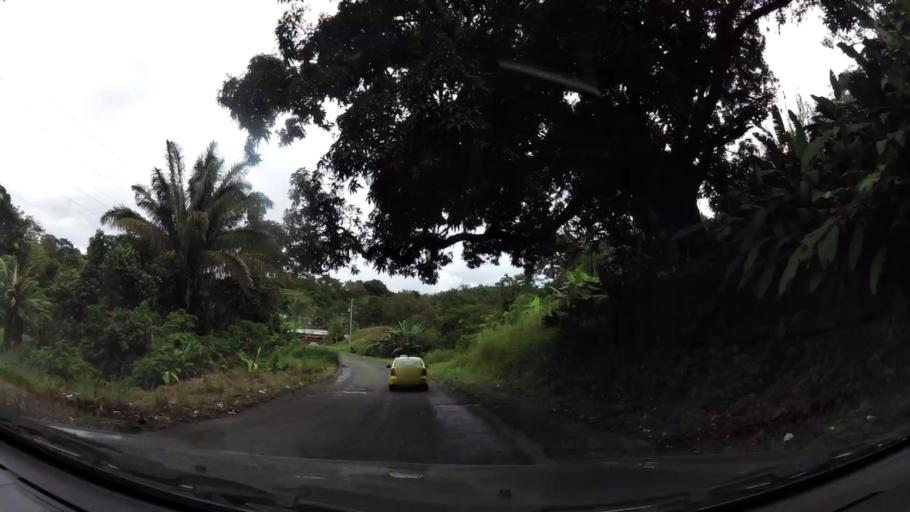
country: PA
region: Panama
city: Chilibre
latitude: 9.1343
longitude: -79.6131
